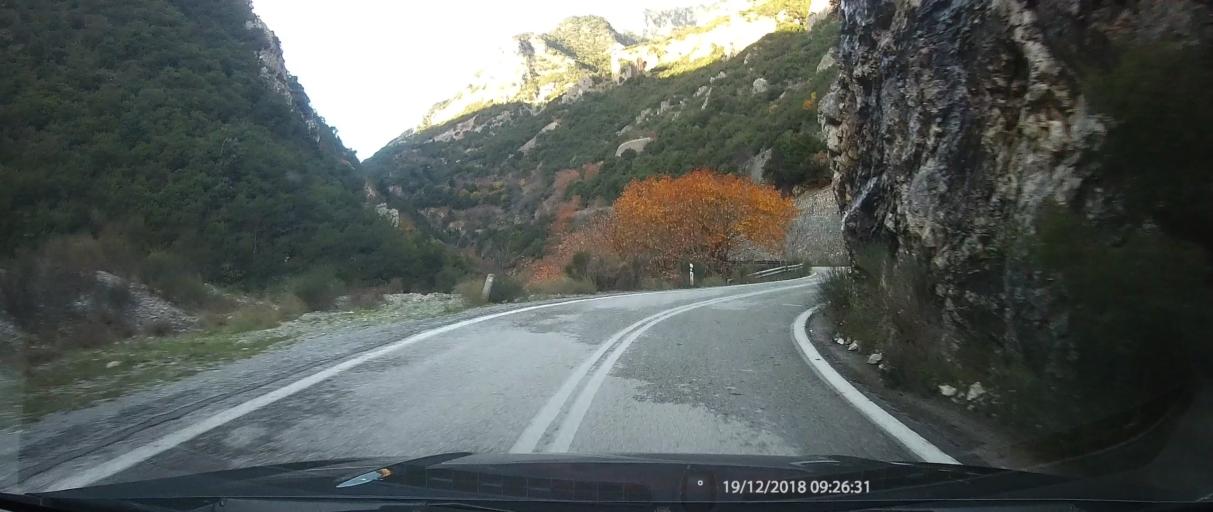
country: GR
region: Peloponnese
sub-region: Nomos Lakonias
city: Magoula
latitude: 37.0926
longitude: 22.3295
